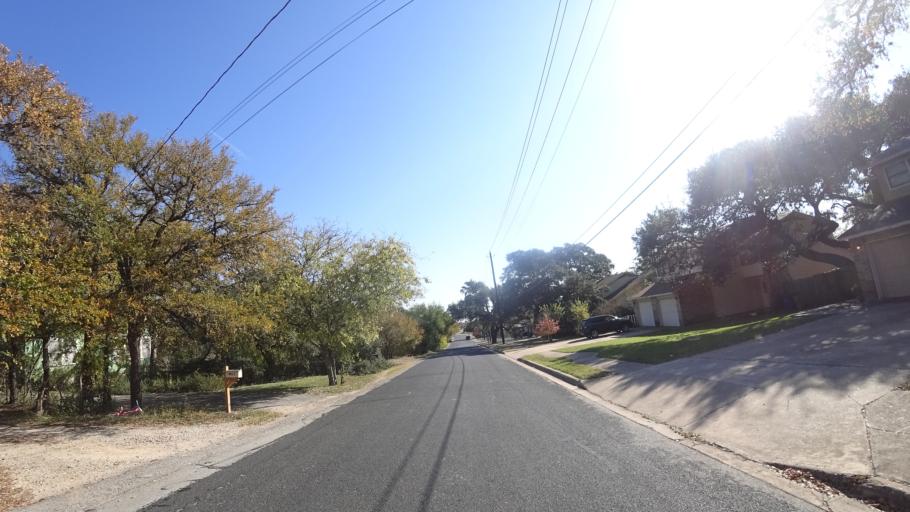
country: US
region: Texas
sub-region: Travis County
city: Barton Creek
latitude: 30.2341
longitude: -97.8496
